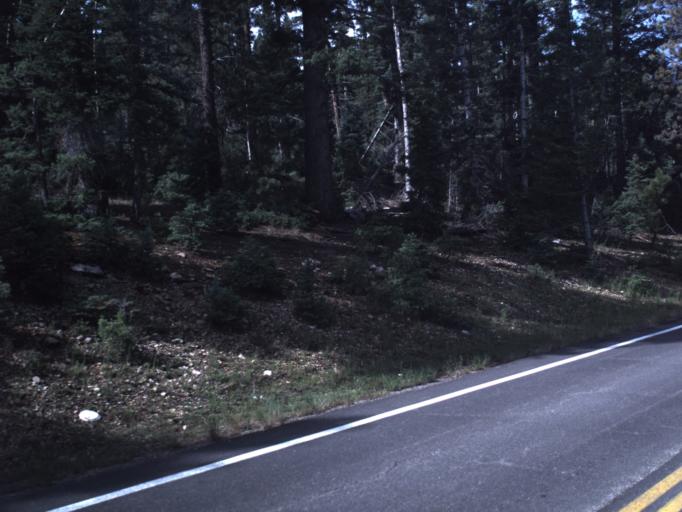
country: US
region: Utah
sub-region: Iron County
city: Parowan
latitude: 37.5173
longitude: -112.6778
